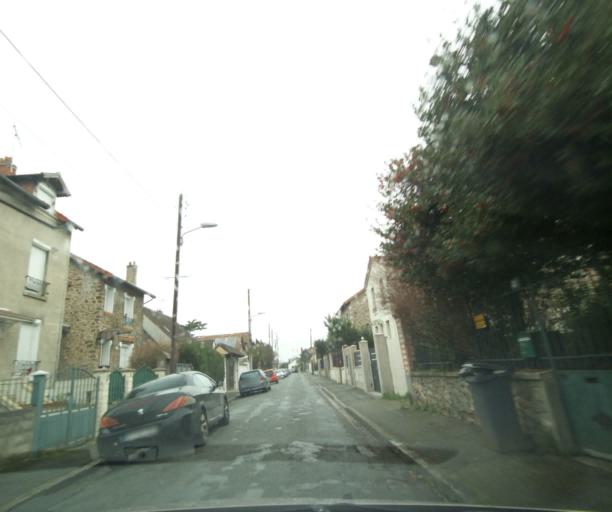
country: FR
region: Ile-de-France
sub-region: Departement du Val-de-Marne
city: Ablon-sur-Seine
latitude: 48.7388
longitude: 2.4214
